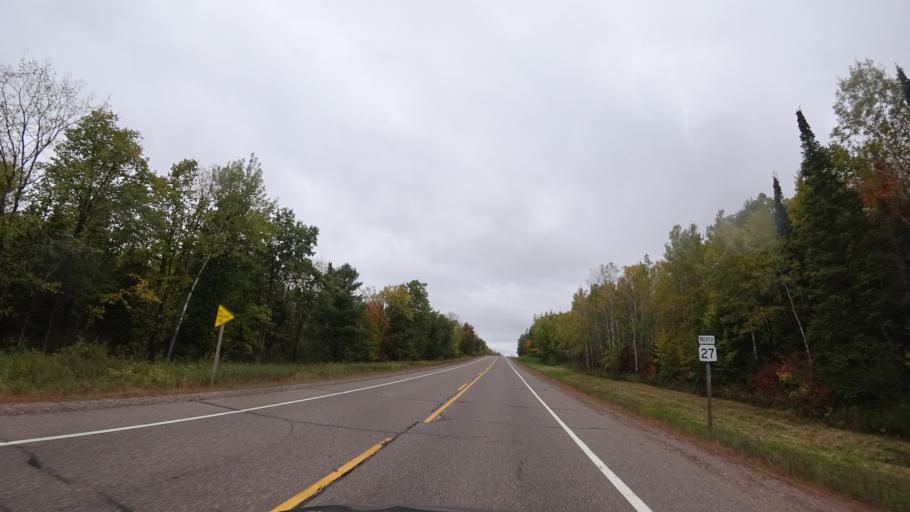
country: US
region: Wisconsin
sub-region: Rusk County
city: Ladysmith
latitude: 45.5745
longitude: -91.1118
